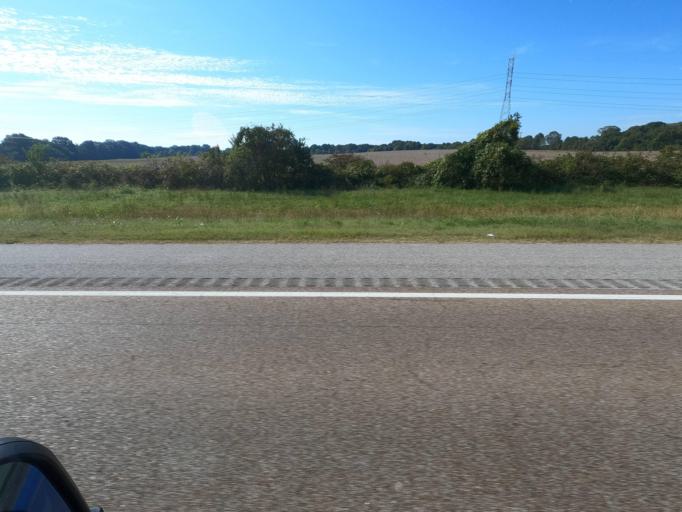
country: US
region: Tennessee
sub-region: Shelby County
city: Millington
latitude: 35.3114
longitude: -89.8592
